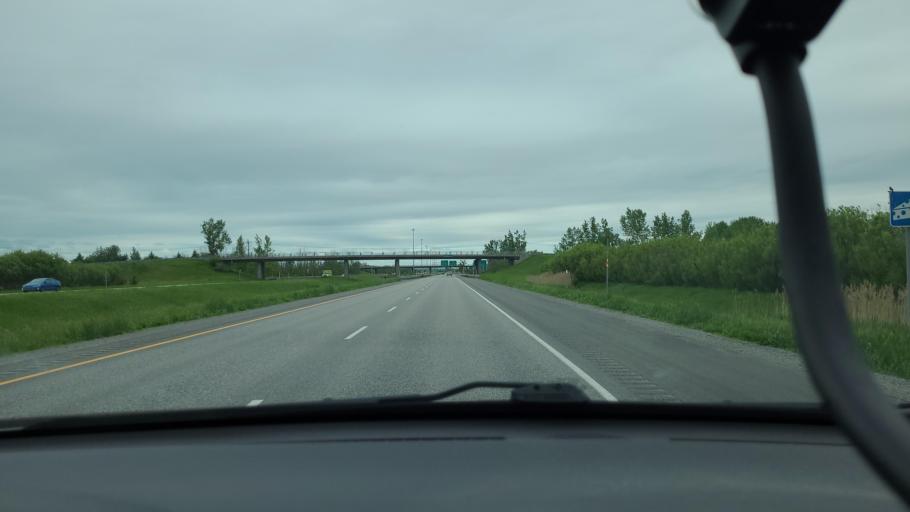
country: CA
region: Quebec
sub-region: Lanaudiere
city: Saint-Lin-Laurentides
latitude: 45.8564
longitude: -73.6498
